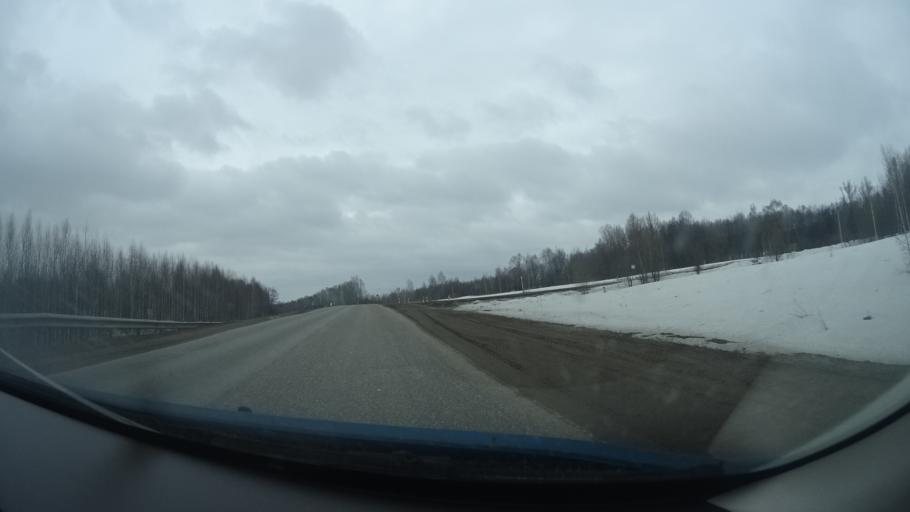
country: RU
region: Bashkortostan
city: Birsk
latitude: 55.2829
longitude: 55.6577
